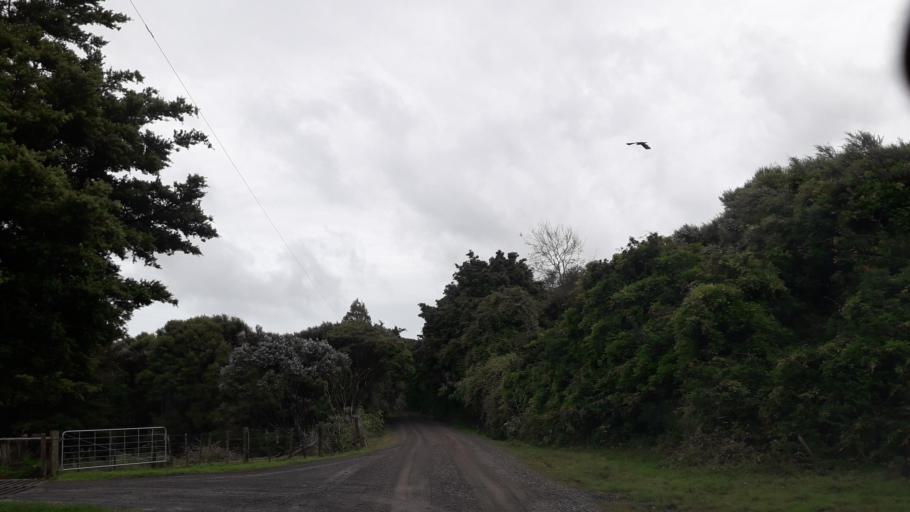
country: NZ
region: Northland
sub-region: Far North District
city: Kaitaia
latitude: -35.3886
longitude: 173.4049
